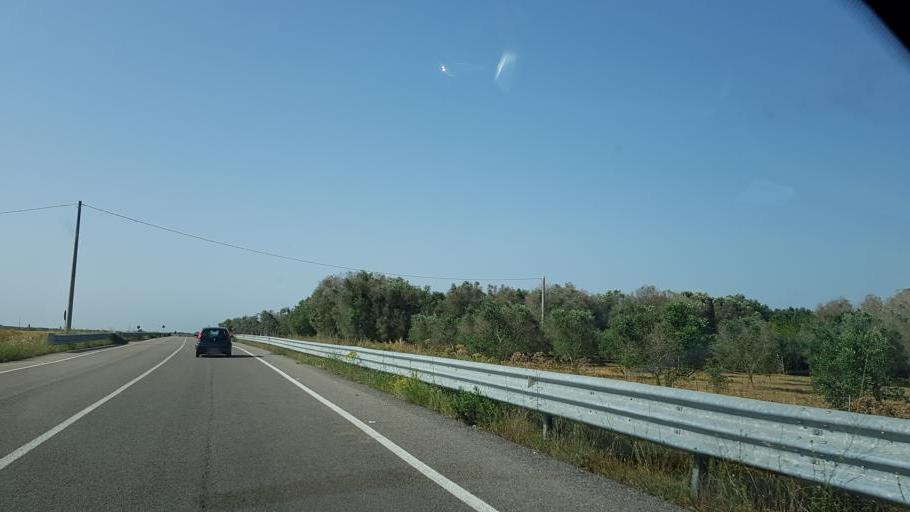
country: IT
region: Apulia
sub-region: Provincia di Brindisi
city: Mesagne
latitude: 40.5071
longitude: 17.8273
